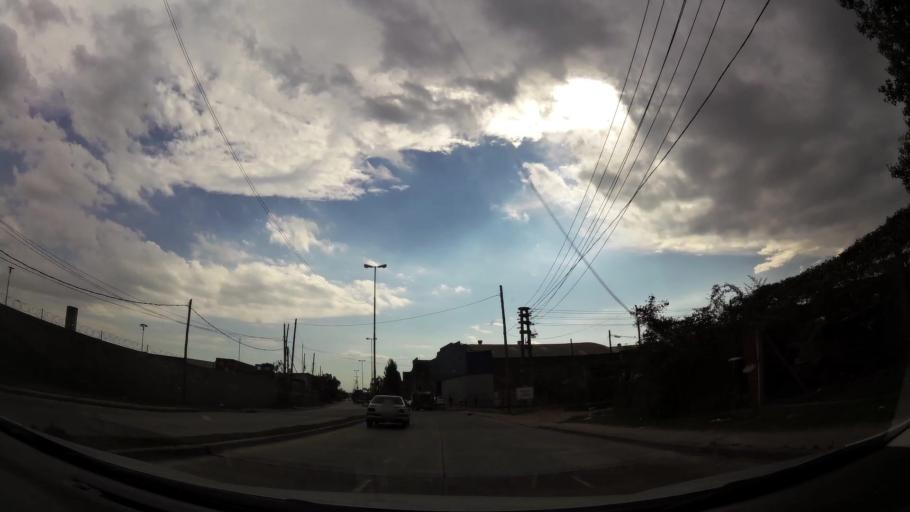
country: AR
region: Buenos Aires
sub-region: Partido de Tigre
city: Tigre
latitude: -34.4809
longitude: -58.6064
